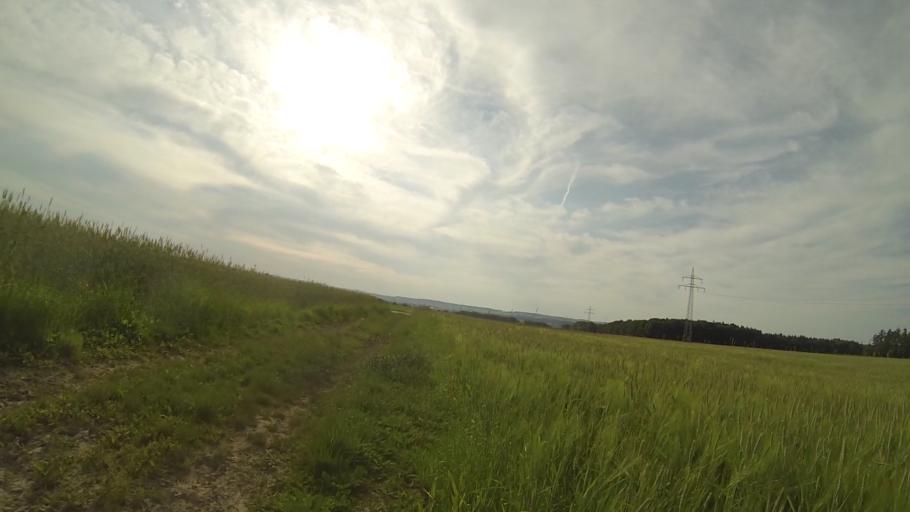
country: DE
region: Baden-Wuerttemberg
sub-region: Tuebingen Region
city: Staig
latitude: 48.3417
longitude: 9.9611
